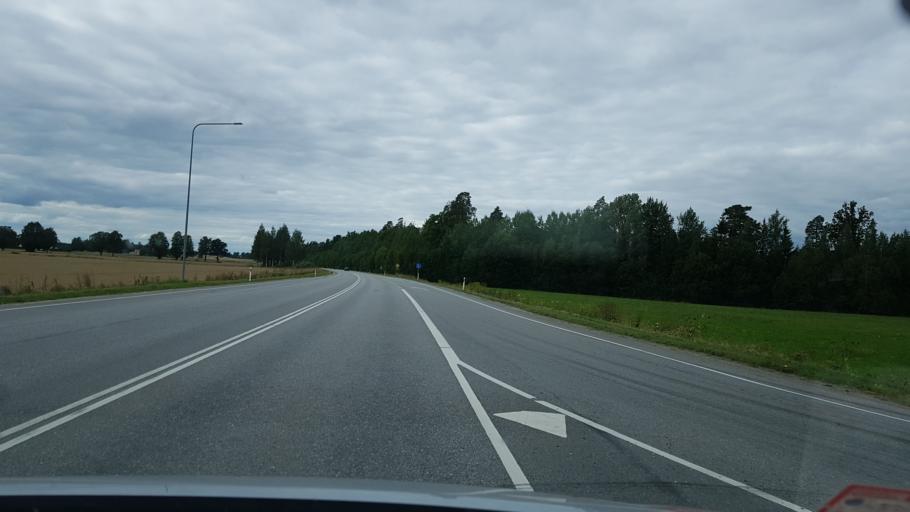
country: EE
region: Tartu
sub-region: Tartu linn
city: Tartu
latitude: 58.3678
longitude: 26.8836
